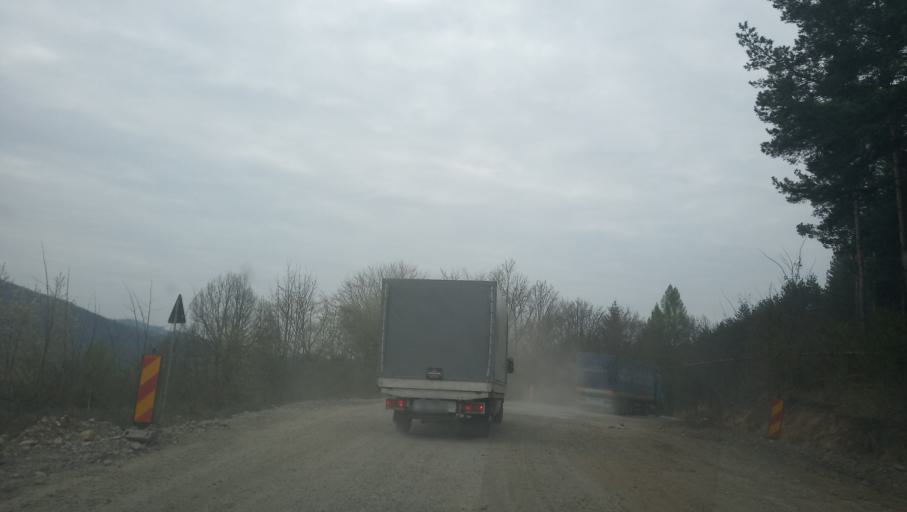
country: RO
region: Arad
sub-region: Comuna Varfurile
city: Varfurile
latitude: 46.3663
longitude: 22.5497
